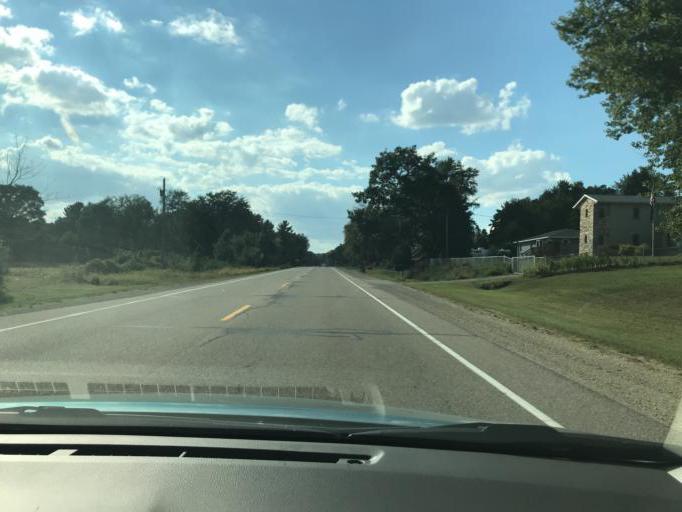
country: US
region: Wisconsin
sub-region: Rock County
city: Orfordville
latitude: 42.5257
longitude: -89.2083
